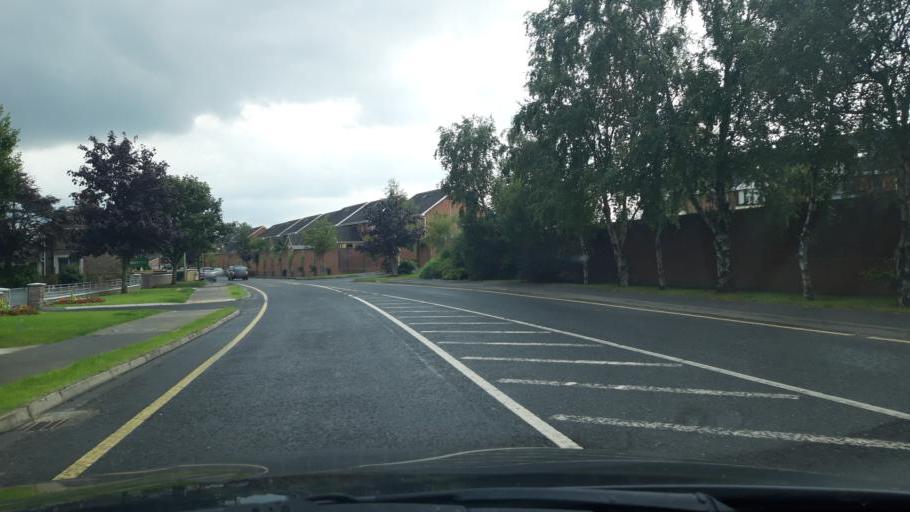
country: IE
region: Leinster
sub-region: Kildare
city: Athy
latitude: 52.9996
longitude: -6.9880
